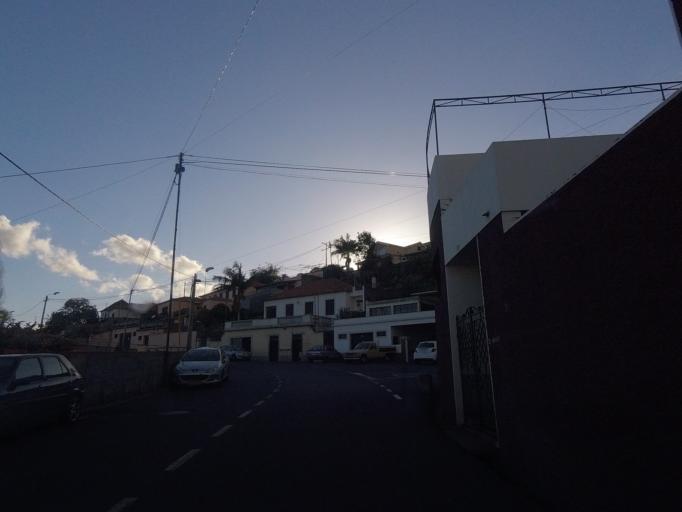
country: PT
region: Madeira
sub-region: Funchal
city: Nossa Senhora do Monte
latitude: 32.6725
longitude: -16.9275
